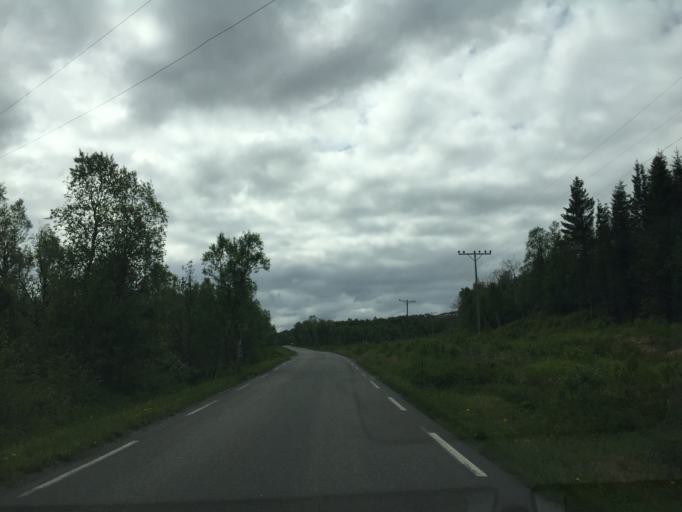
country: NO
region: Nordland
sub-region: Bodo
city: Loding
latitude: 67.3037
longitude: 14.6274
